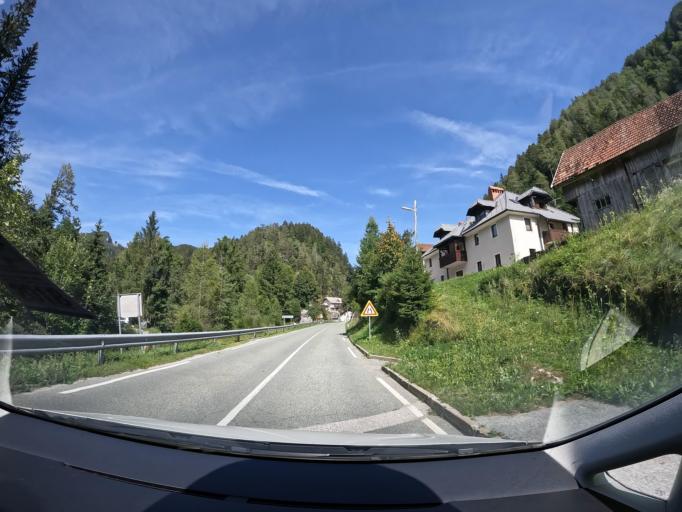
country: SI
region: Jesenice
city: Slovenski Javornik
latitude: 46.4340
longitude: 14.0964
